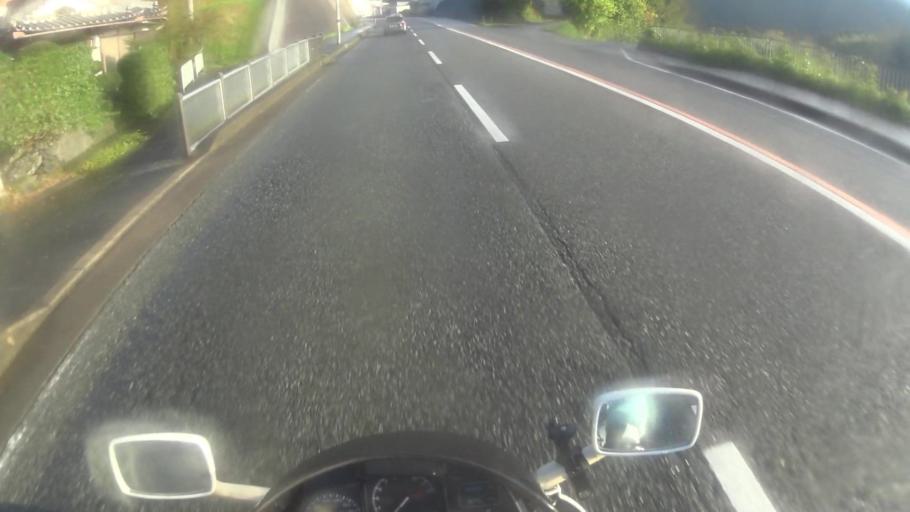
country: JP
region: Kyoto
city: Ayabe
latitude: 35.2250
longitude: 135.2255
